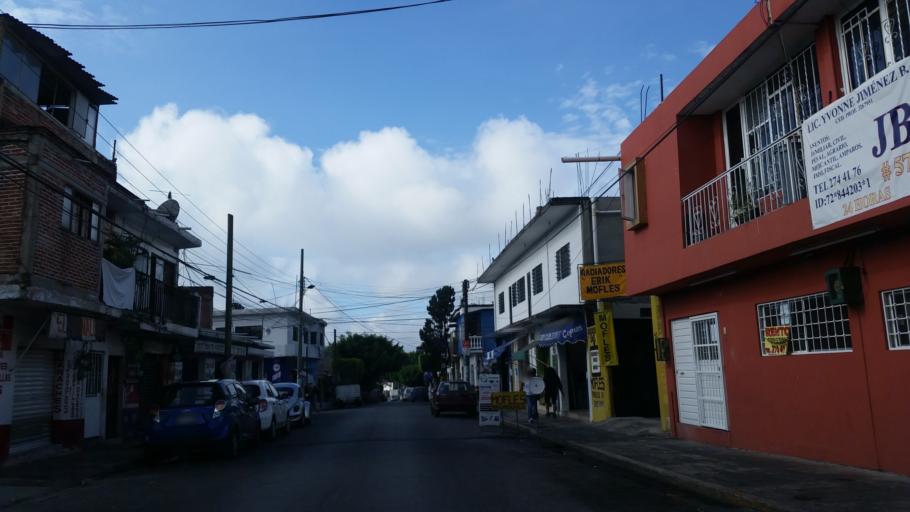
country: MX
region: Morelos
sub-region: Cuernavaca
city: Cuernavaca
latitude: 18.9177
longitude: -99.2066
